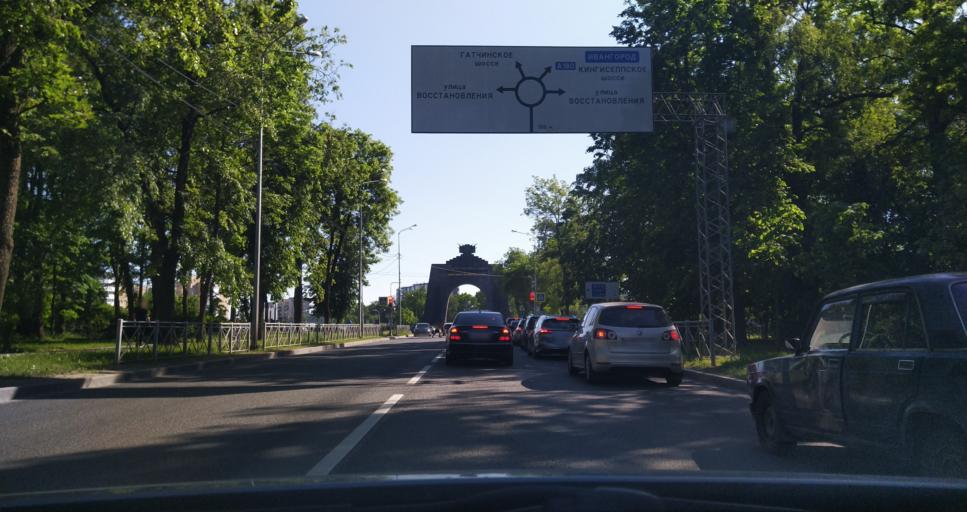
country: RU
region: St.-Petersburg
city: Krasnoye Selo
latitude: 59.7258
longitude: 30.0811
